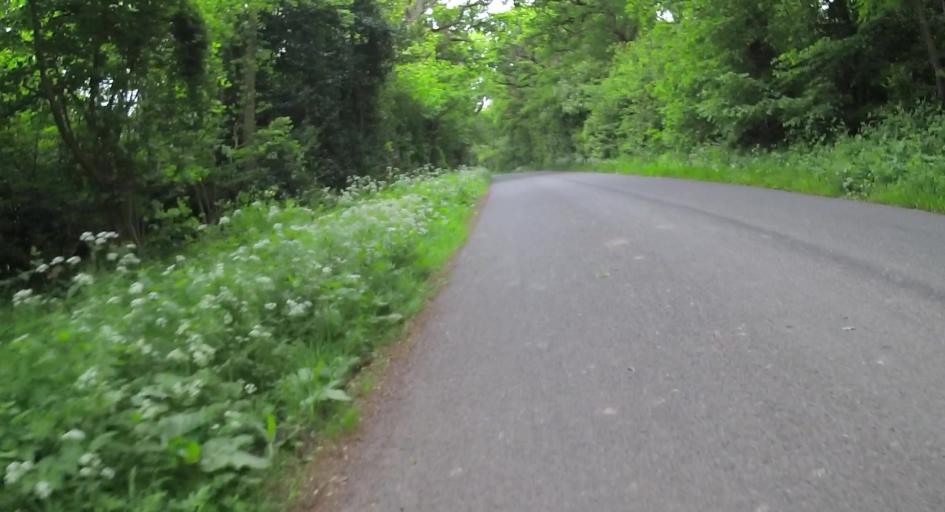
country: GB
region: England
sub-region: West Berkshire
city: Stratfield Mortimer
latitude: 51.3682
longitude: -1.0316
